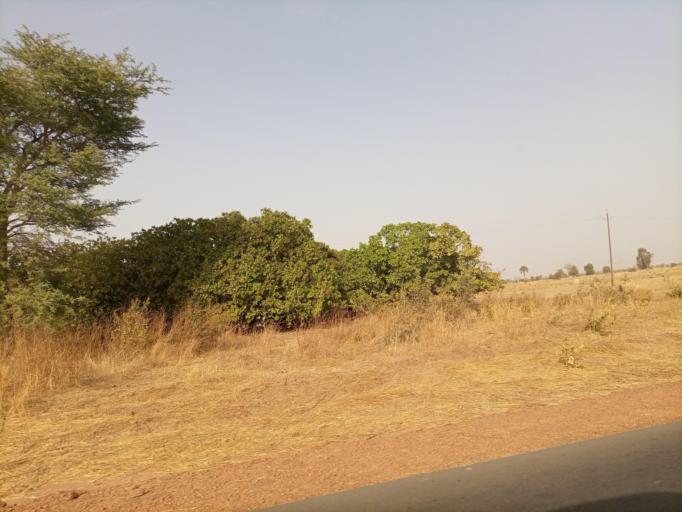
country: SN
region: Fatick
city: Passi
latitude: 14.0426
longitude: -16.3230
